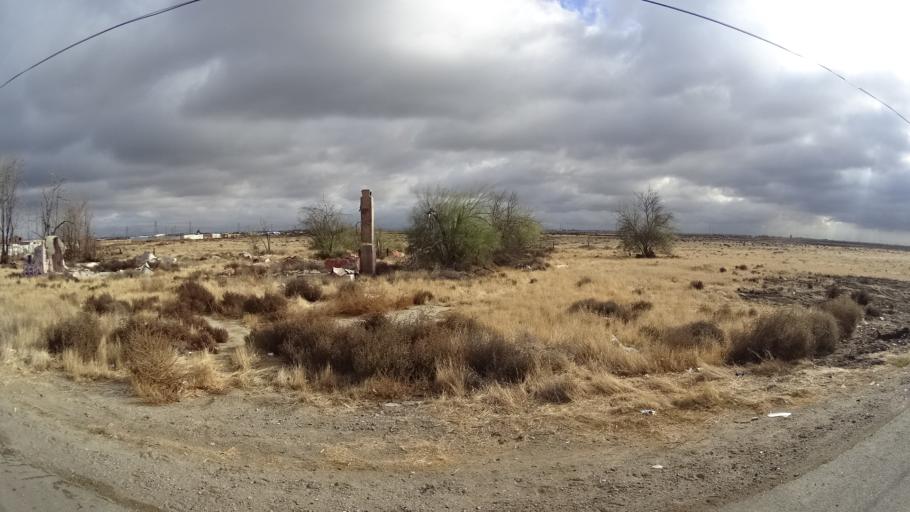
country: US
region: California
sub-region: Kern County
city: Greenfield
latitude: 35.3097
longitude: -118.9854
